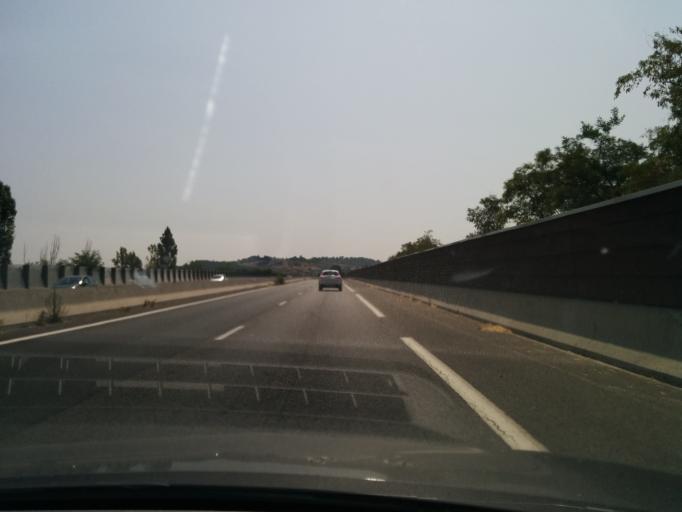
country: FR
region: Midi-Pyrenees
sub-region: Departement du Tarn
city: Le Sequestre
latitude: 43.9124
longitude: 2.1279
